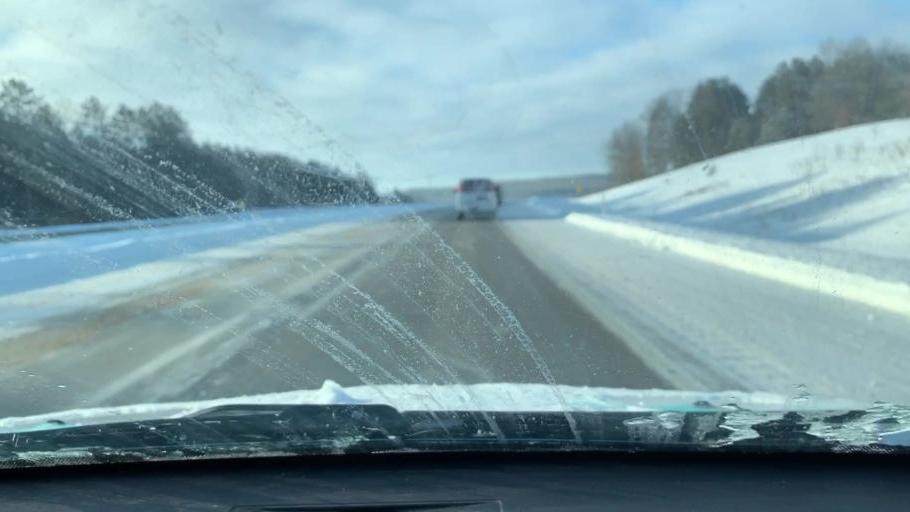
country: US
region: Michigan
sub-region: Wexford County
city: Cadillac
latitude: 44.2386
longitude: -85.3702
